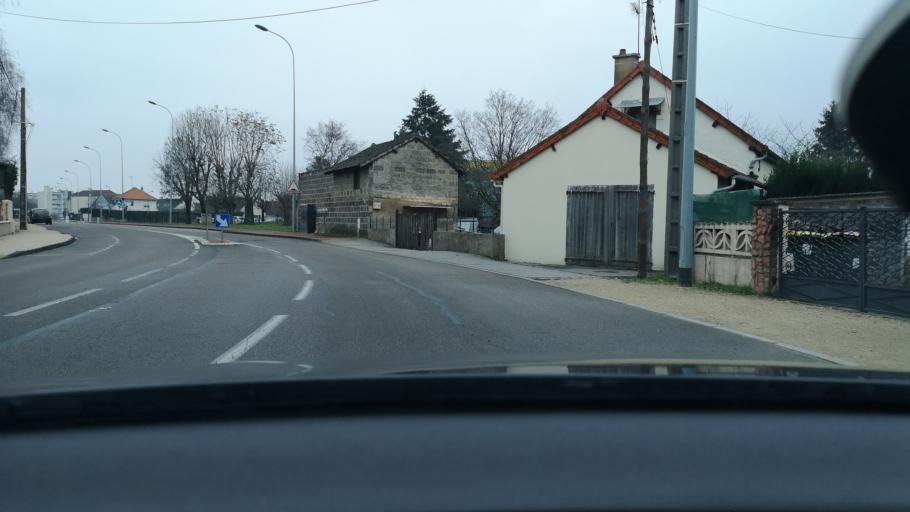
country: FR
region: Bourgogne
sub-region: Departement de Saone-et-Loire
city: Chalon-sur-Saone
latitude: 46.8030
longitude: 4.8533
